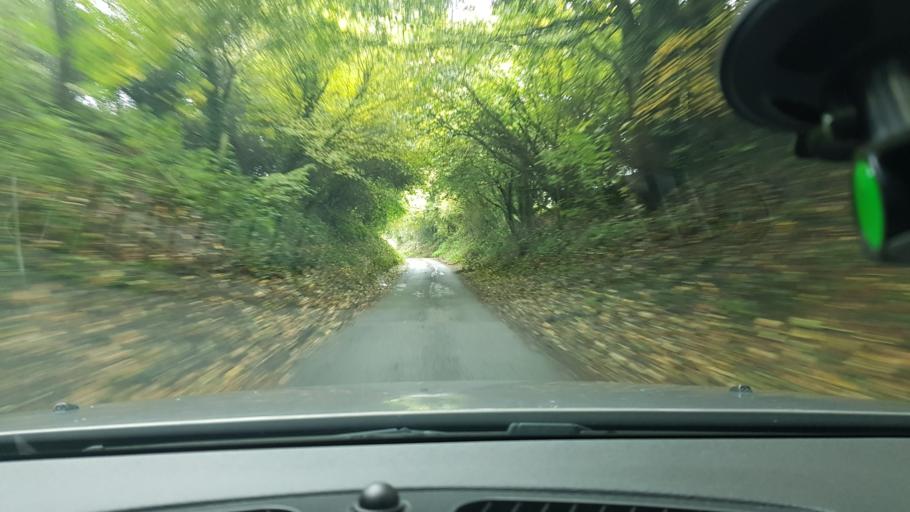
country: GB
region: England
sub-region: Wiltshire
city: Burbage
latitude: 51.3538
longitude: -1.7009
